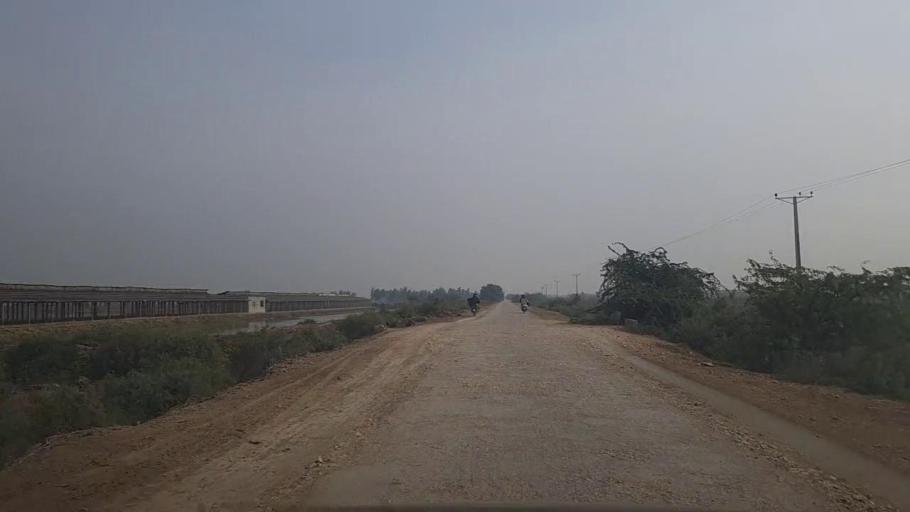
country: PK
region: Sindh
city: Mirpur Sakro
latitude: 24.4568
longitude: 67.7020
